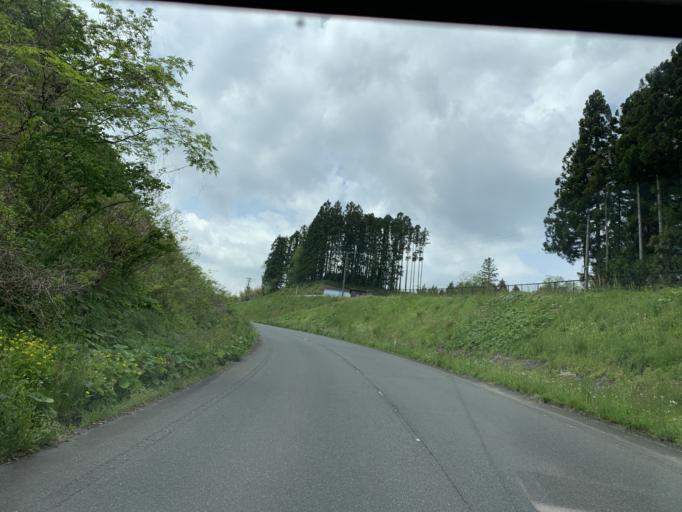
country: JP
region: Miyagi
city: Furukawa
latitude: 38.7295
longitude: 140.9265
